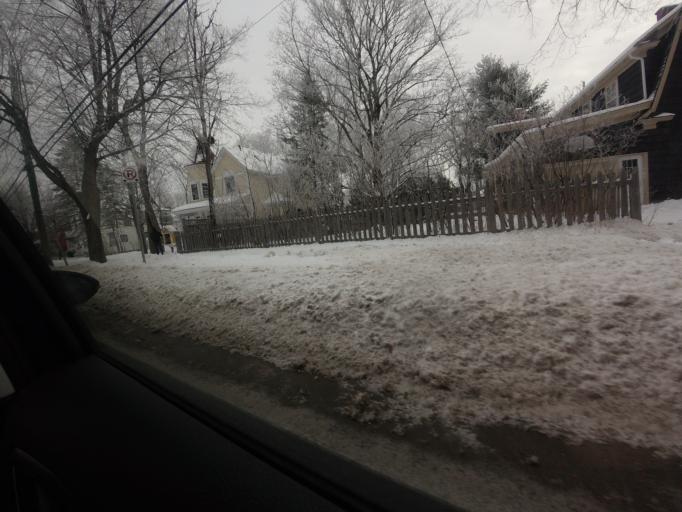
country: CA
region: New Brunswick
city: Fredericton
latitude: 45.9501
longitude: -66.6386
